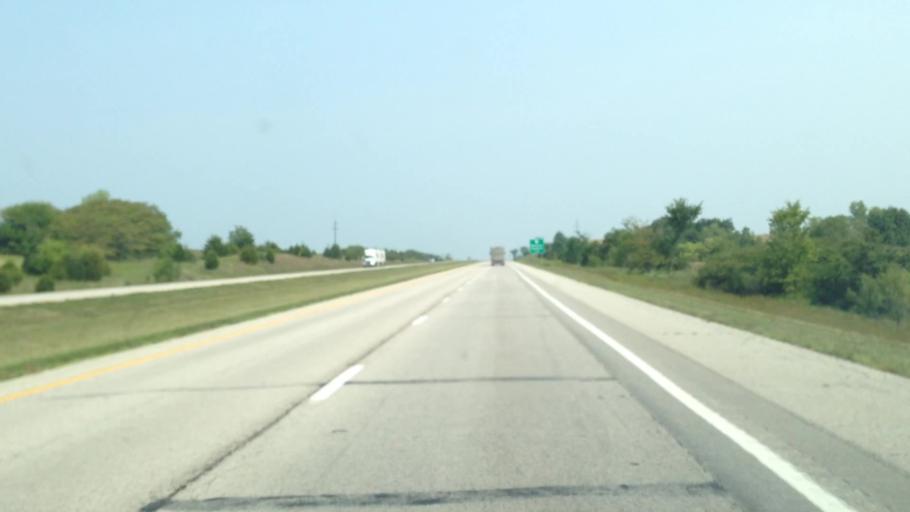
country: US
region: Missouri
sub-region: Harrison County
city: Bethany
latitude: 40.1905
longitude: -94.0142
